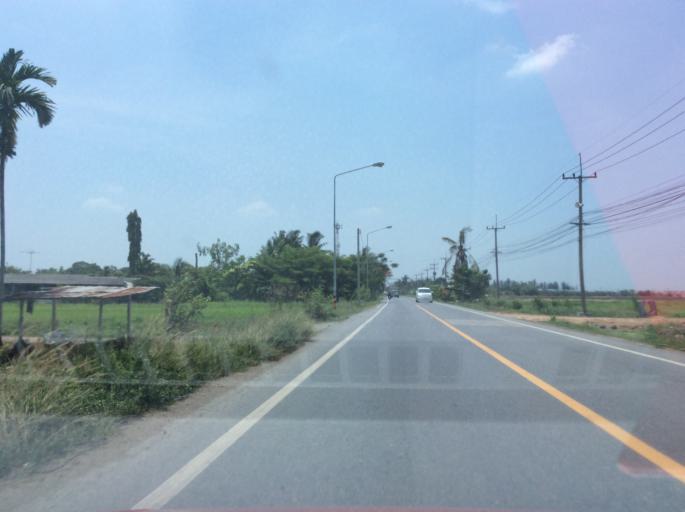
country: TH
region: Pathum Thani
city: Ban Lam Luk Ka
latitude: 14.0058
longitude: 100.7793
